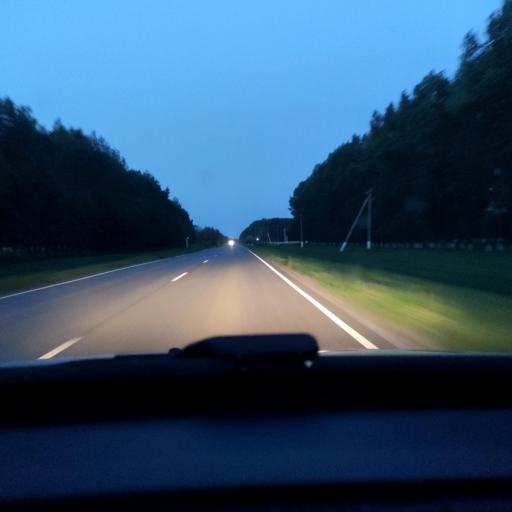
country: RU
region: Voronezj
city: Panino
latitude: 51.6635
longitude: 39.9777
